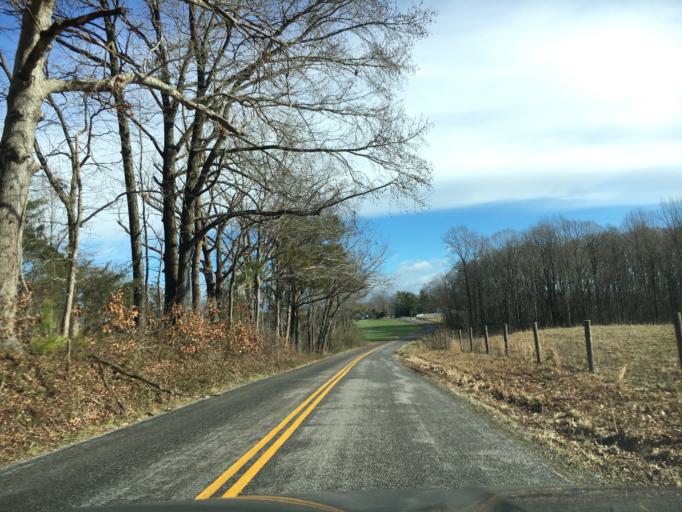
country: US
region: Virginia
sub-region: Amelia County
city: Amelia Court House
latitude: 37.4333
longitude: -78.0546
